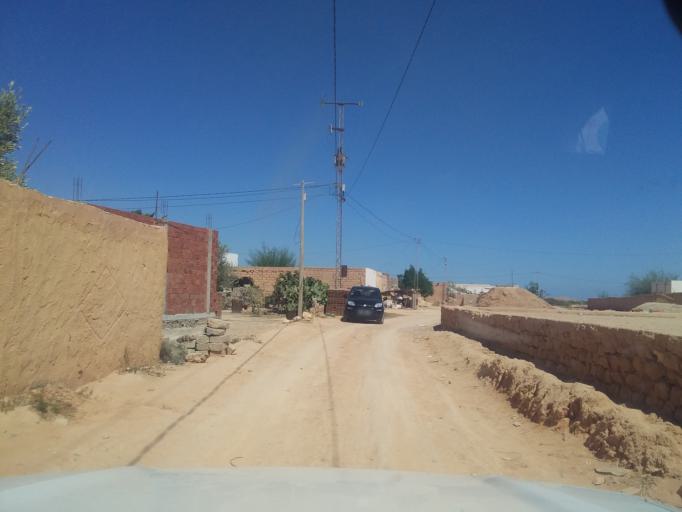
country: TN
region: Qabis
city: Matmata
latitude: 33.5143
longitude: 10.2188
